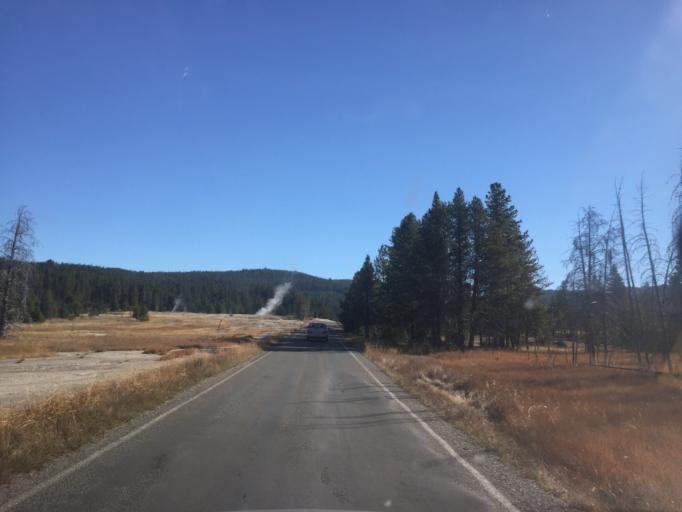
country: US
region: Montana
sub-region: Gallatin County
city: West Yellowstone
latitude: 44.5423
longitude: -110.7980
